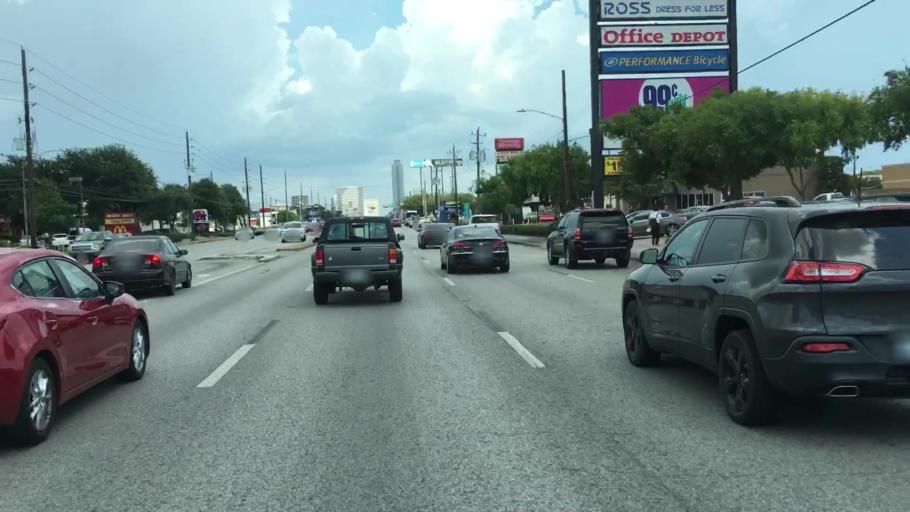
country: US
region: Texas
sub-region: Harris County
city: Piney Point Village
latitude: 29.7375
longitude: -95.5033
